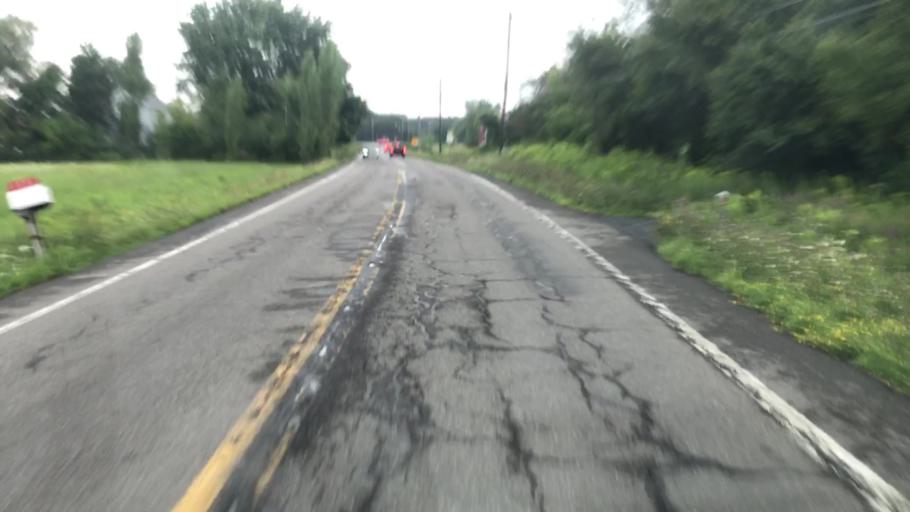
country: US
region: New York
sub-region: Onondaga County
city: Skaneateles
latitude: 42.9695
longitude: -76.4292
